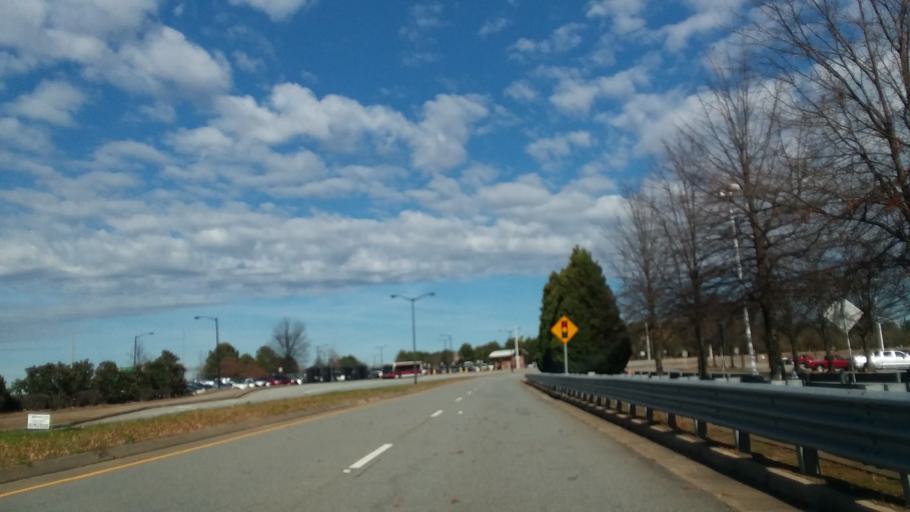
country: US
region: Georgia
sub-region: Gwinnett County
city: Duluth
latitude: 33.9817
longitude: -84.0851
